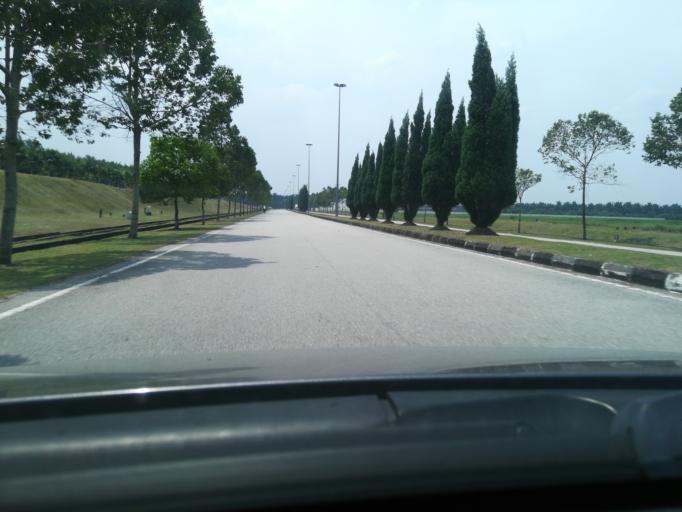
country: MY
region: Kedah
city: Kulim
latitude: 5.4260
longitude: 100.5775
